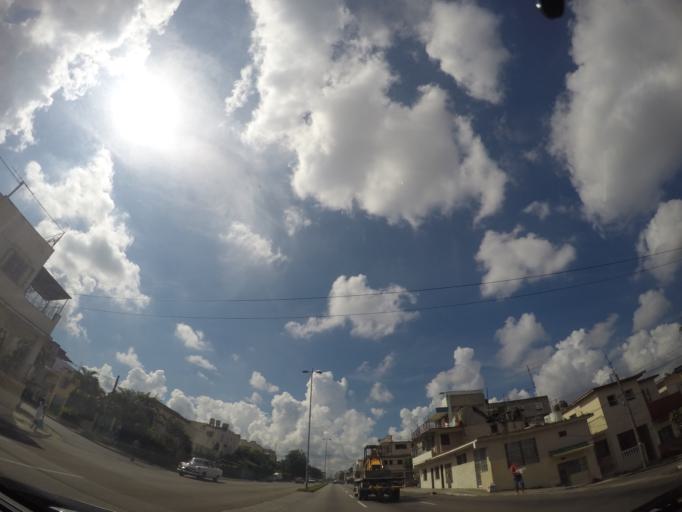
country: CU
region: La Habana
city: Cerro
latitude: 23.0983
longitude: -82.4212
